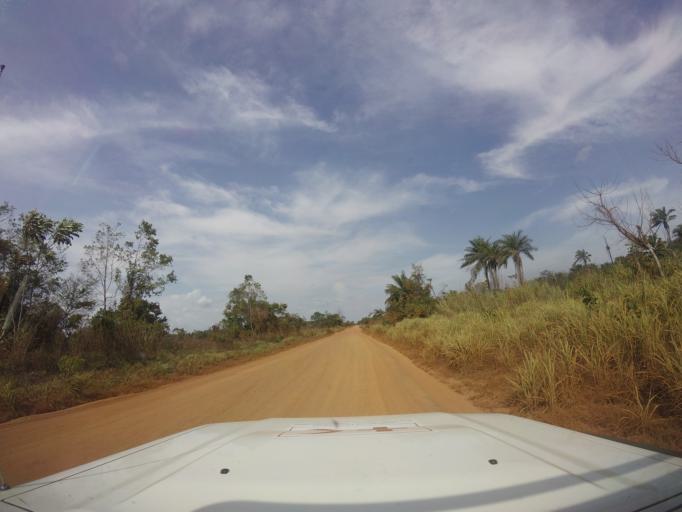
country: LR
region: Grand Cape Mount
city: Robertsport
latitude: 6.6839
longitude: -11.1271
